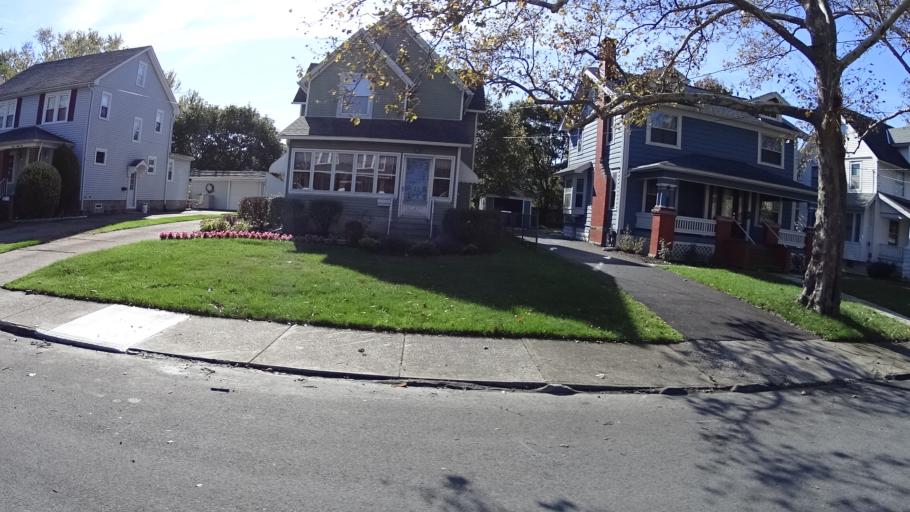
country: US
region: Ohio
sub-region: Lorain County
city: Lorain
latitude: 41.4619
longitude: -82.1827
